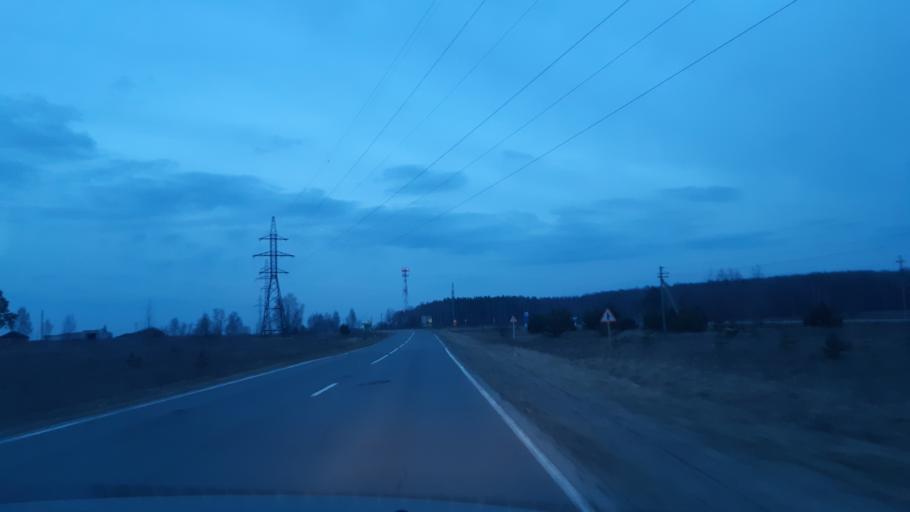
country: RU
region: Vladimir
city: Luknovo
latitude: 56.1962
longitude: 42.0323
